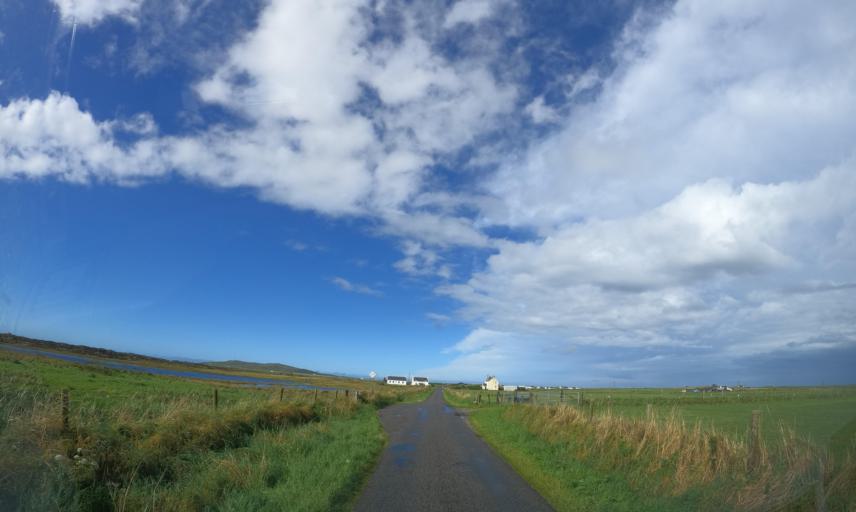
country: GB
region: Scotland
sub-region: Eilean Siar
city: Barra
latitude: 56.5211
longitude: -6.8993
